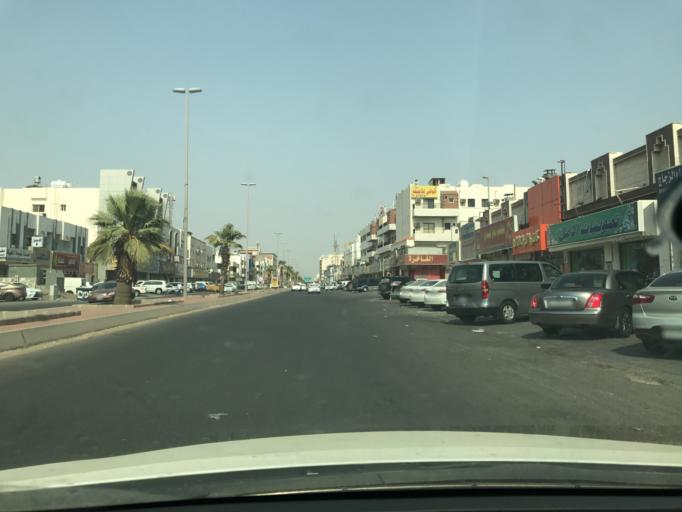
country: SA
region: Makkah
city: Jeddah
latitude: 21.6144
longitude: 39.1586
